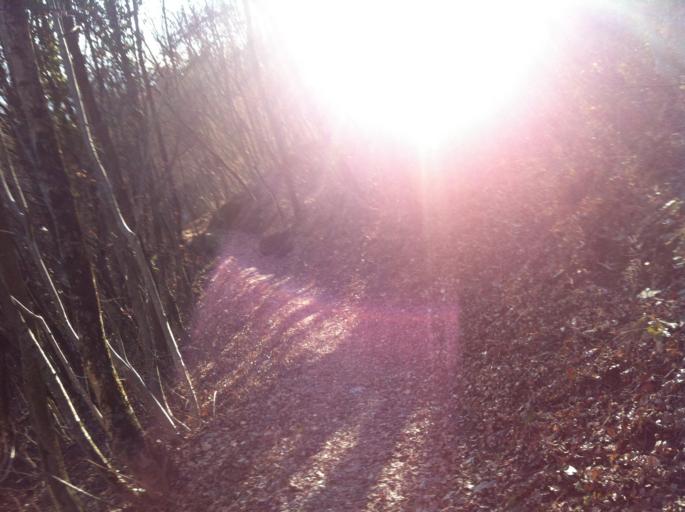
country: IT
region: Trentino-Alto Adige
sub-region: Bolzano
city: Bressanone
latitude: 46.7213
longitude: 11.6677
